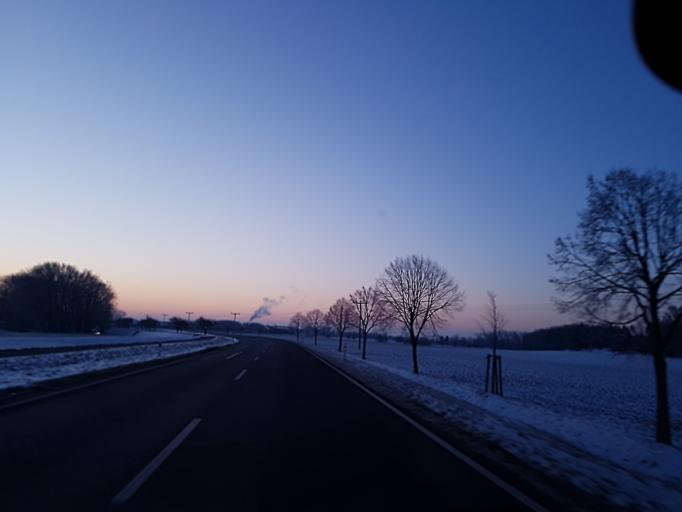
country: DE
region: Brandenburg
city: Muhlberg
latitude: 51.4110
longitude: 13.1822
